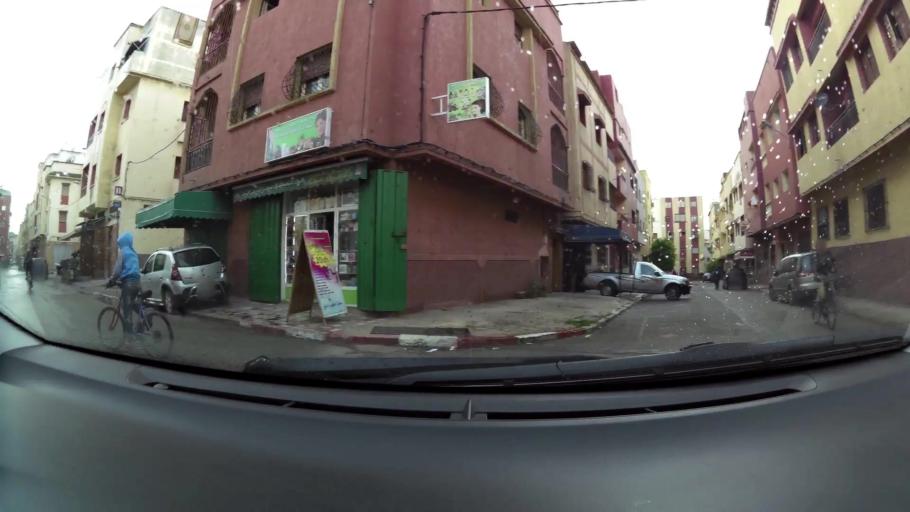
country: MA
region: Grand Casablanca
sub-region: Mohammedia
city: Mohammedia
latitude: 33.6758
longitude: -7.3919
